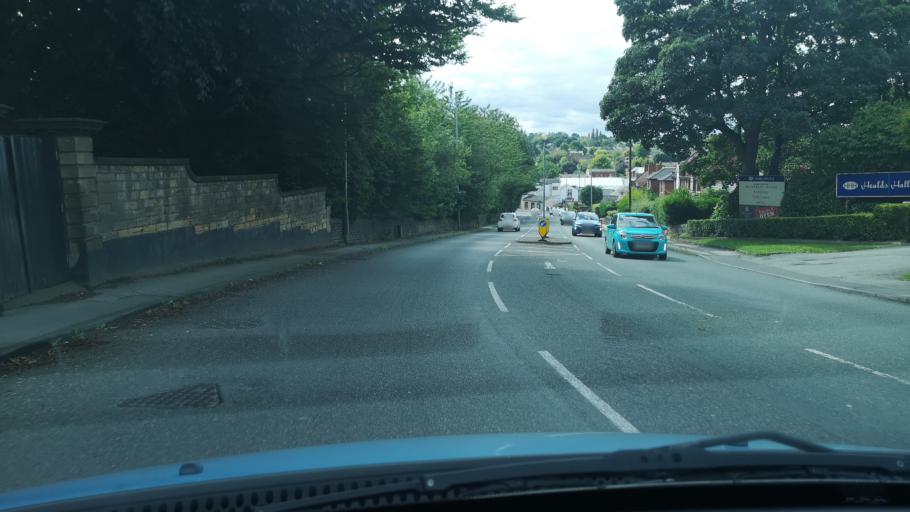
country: GB
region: England
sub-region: Kirklees
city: Heckmondwike
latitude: 53.7115
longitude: -1.6841
